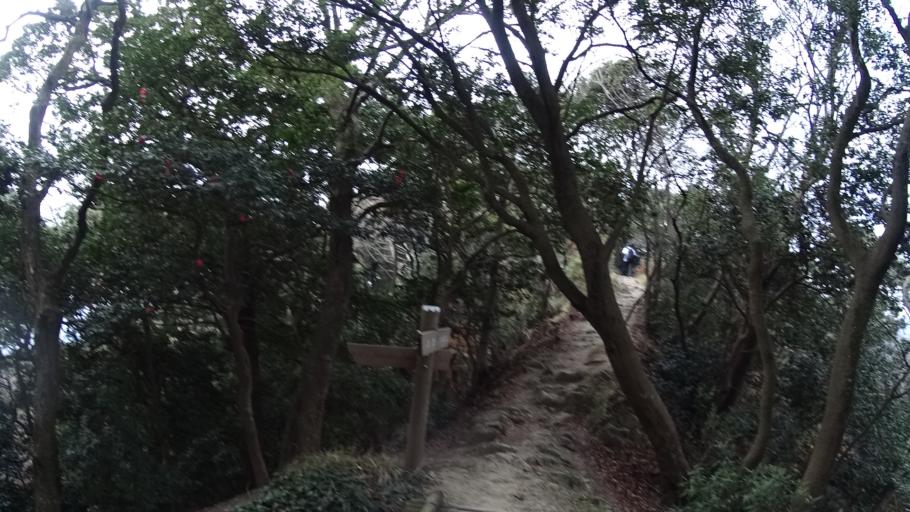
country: JP
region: Kanagawa
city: Hiratsuka
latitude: 35.3227
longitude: 139.3204
